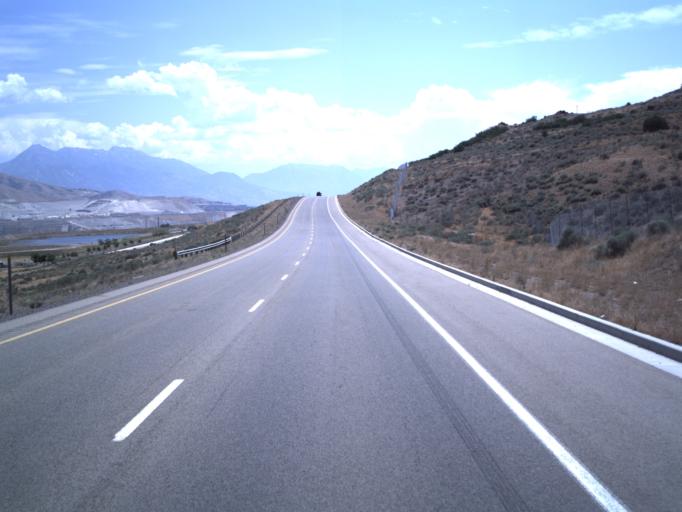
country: US
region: Utah
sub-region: Salt Lake County
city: Bluffdale
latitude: 40.4720
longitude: -111.9725
